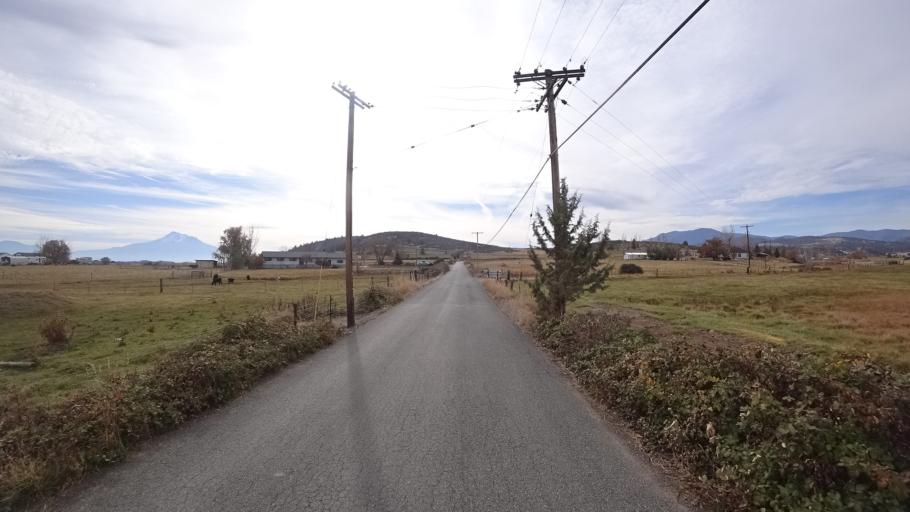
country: US
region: California
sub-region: Siskiyou County
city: Montague
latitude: 41.7008
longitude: -122.5496
